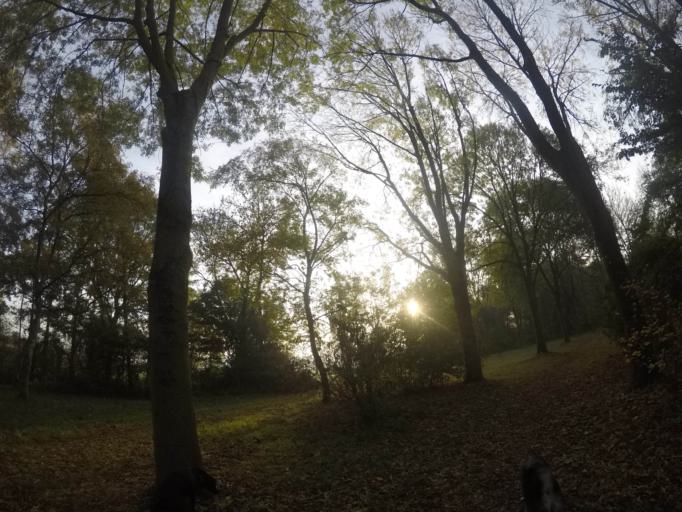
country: NL
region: Gelderland
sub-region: Gemeente Zevenaar
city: Zevenaar
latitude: 51.9196
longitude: 6.0794
